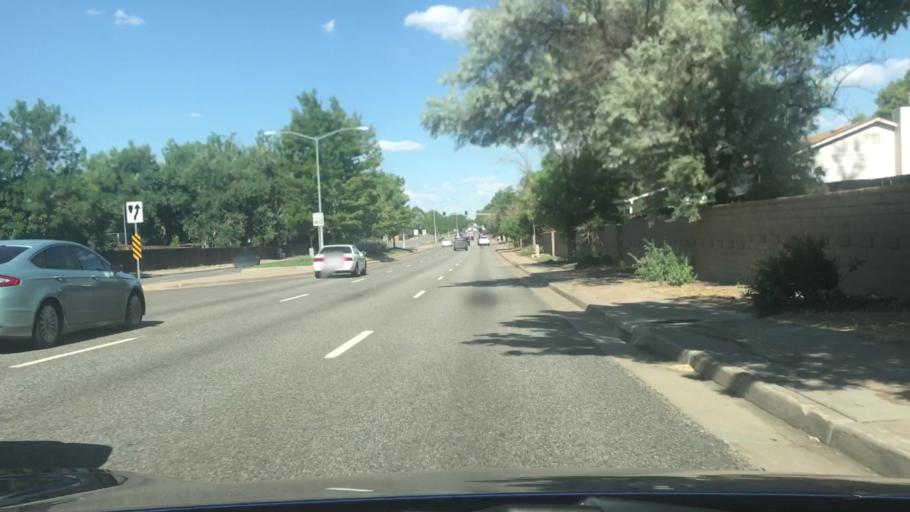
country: US
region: Colorado
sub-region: Arapahoe County
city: Dove Valley
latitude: 39.6530
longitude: -104.7996
